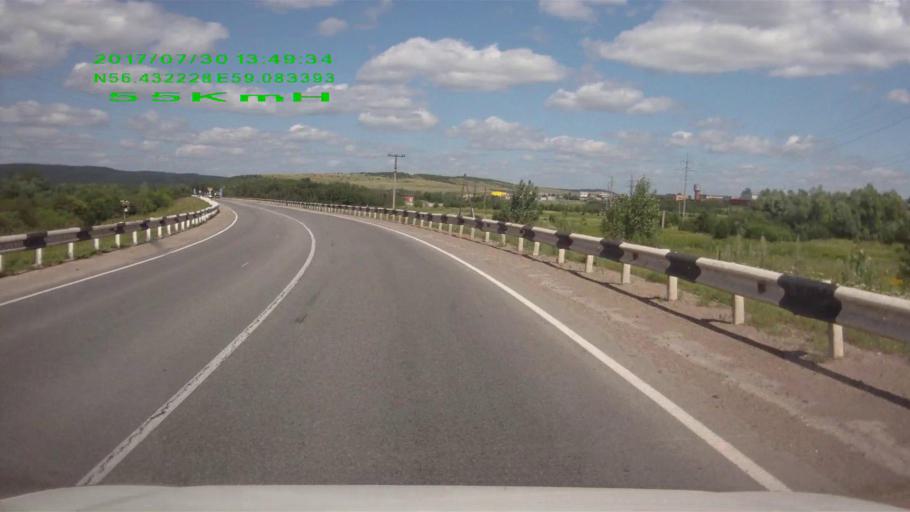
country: RU
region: Sverdlovsk
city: Mikhaylovsk
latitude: 56.4323
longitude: 59.0836
